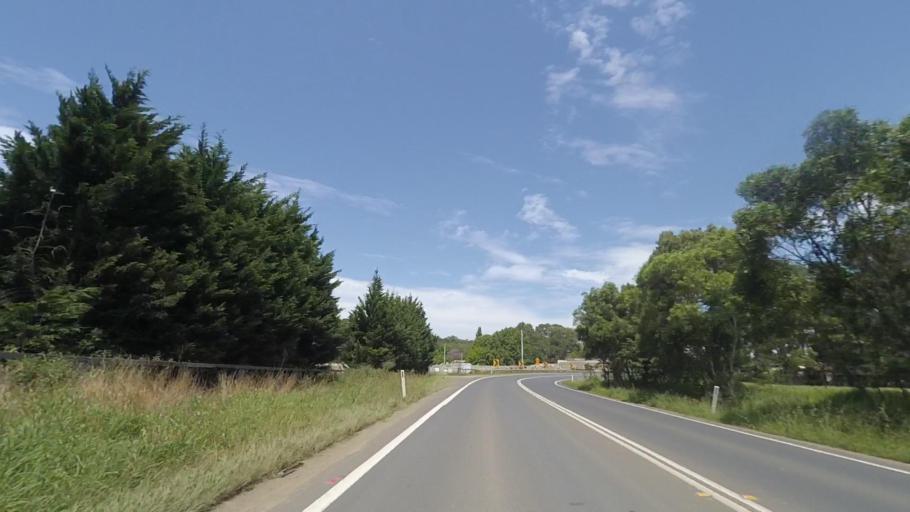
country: AU
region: New South Wales
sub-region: Kiama
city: Gerringong
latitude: -34.7448
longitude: 150.7598
